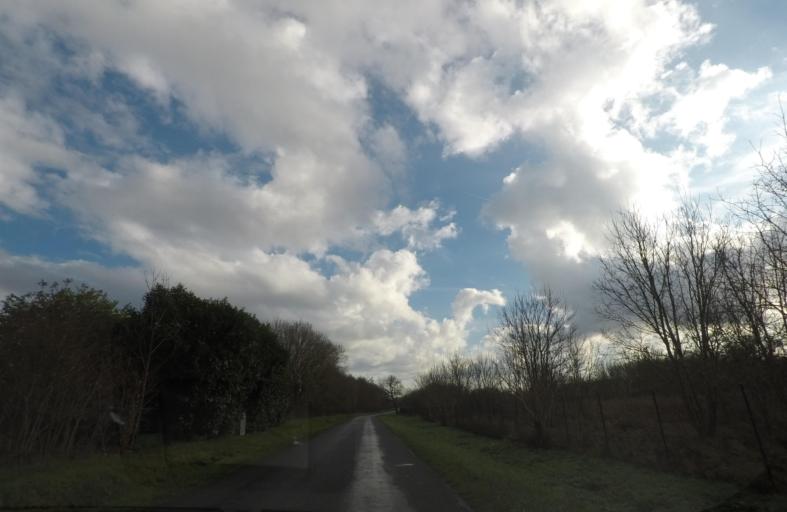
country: FR
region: Centre
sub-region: Departement du Cher
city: Bourges
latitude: 47.0480
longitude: 2.4170
